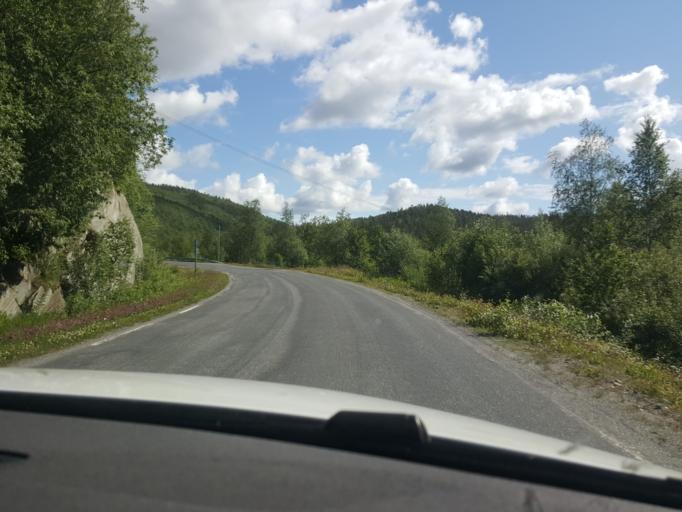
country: NO
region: Nordland
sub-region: Saltdal
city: Rognan
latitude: 67.0371
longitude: 15.0183
